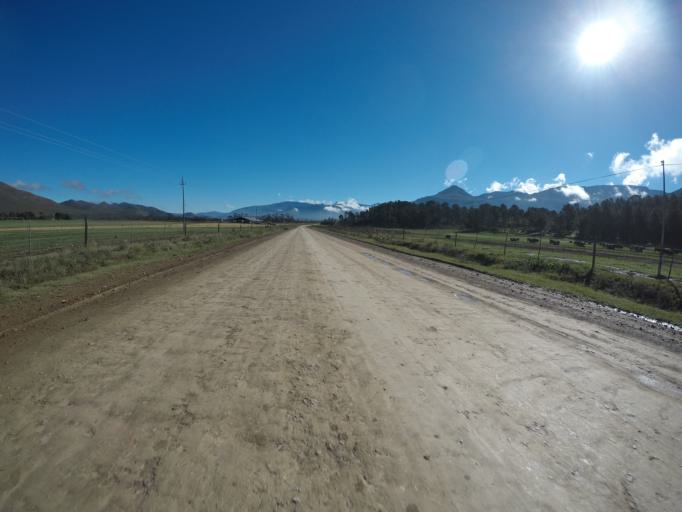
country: ZA
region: Western Cape
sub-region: Overberg District Municipality
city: Caledon
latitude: -34.0721
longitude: 19.6369
